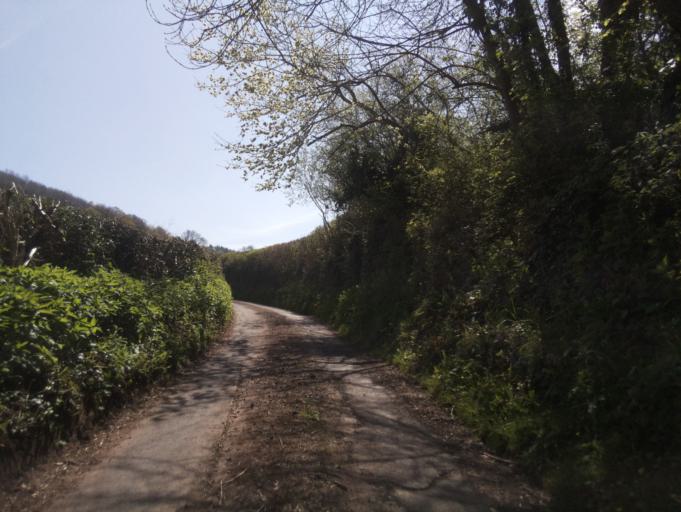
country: GB
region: Wales
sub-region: Monmouthshire
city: Llangwm
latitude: 51.6873
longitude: -2.8163
